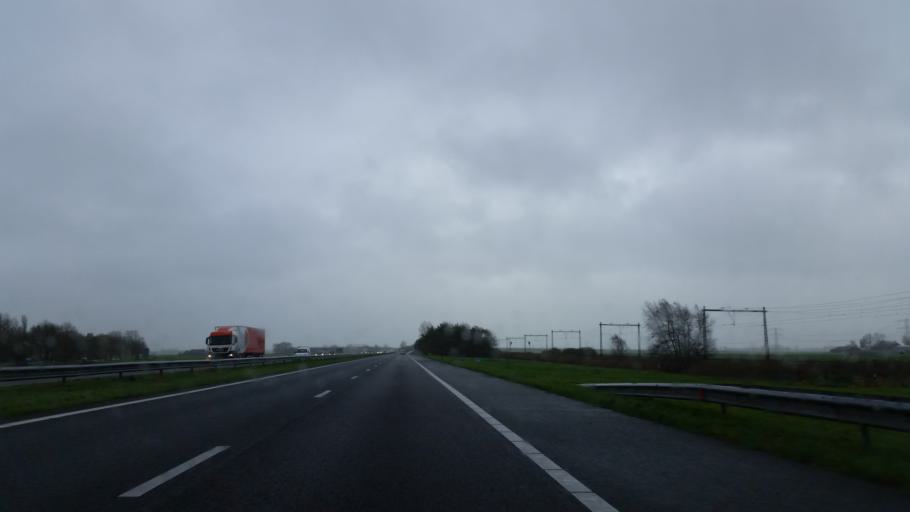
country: NL
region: Friesland
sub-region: Gemeente Boarnsterhim
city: Reduzum
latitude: 53.1236
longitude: 5.8064
